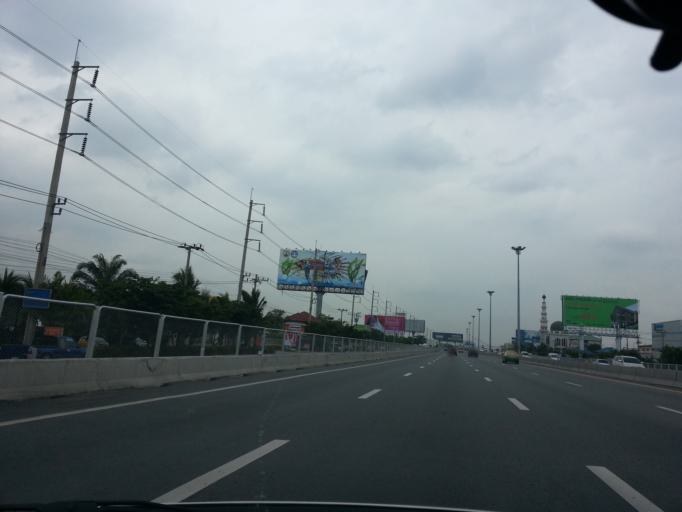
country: TH
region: Bangkok
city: Suan Luang
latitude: 13.7374
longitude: 100.6619
